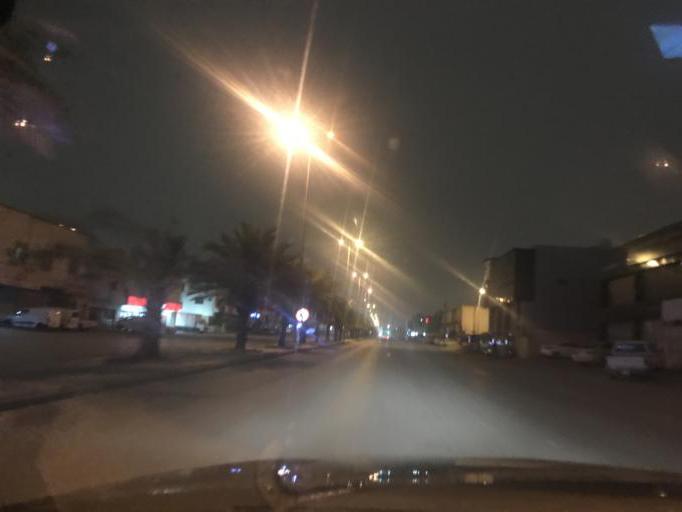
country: SA
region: Ar Riyad
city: Riyadh
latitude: 24.7511
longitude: 46.7809
